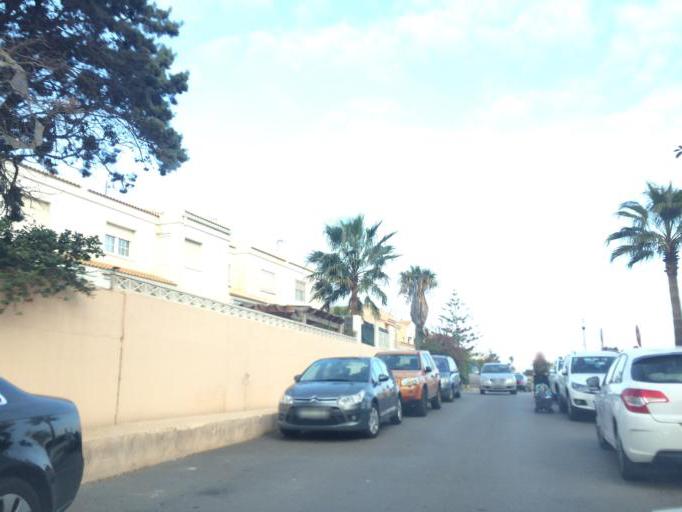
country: ES
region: Andalusia
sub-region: Provincia de Almeria
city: Almeria
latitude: 36.8203
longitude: -2.4357
